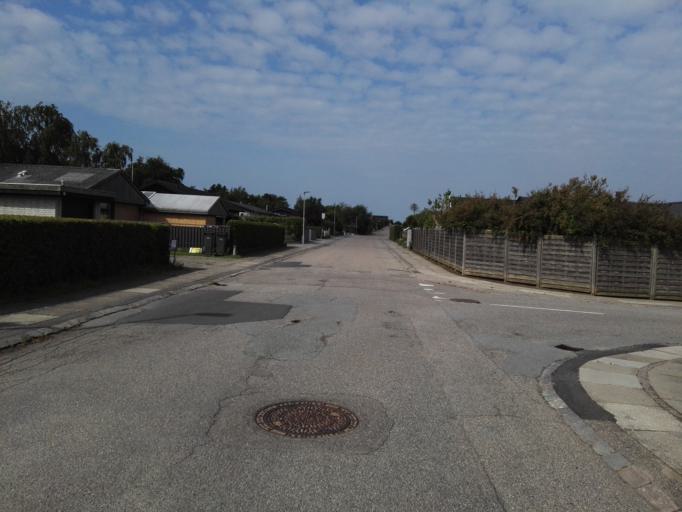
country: DK
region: Capital Region
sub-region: Egedal Kommune
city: Olstykke
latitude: 55.7865
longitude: 12.1397
